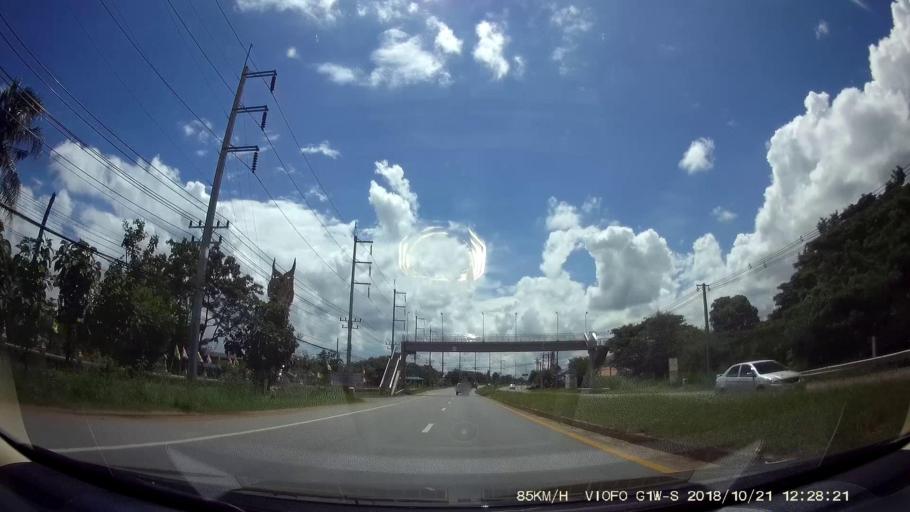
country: TH
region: Nakhon Ratchasima
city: Dan Khun Thot
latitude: 15.1905
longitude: 101.7608
